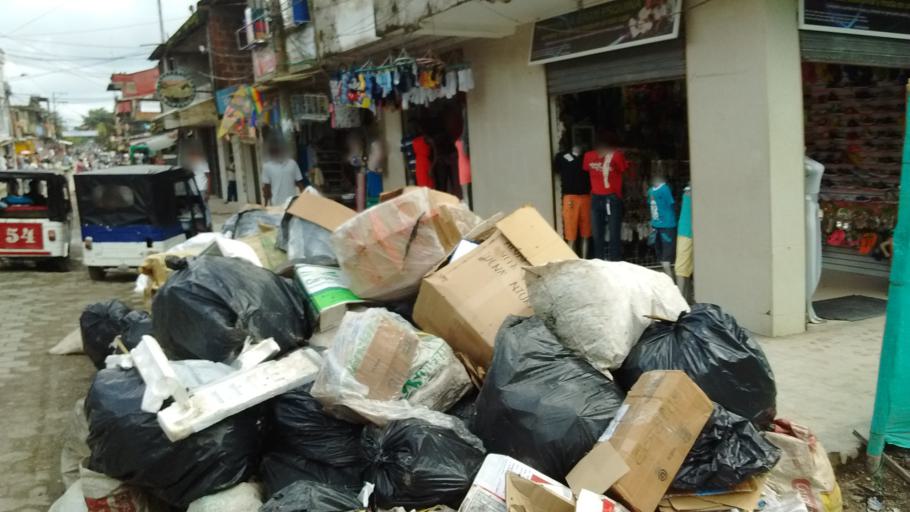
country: CO
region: Cauca
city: Guapi
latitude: 2.5719
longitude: -77.8838
